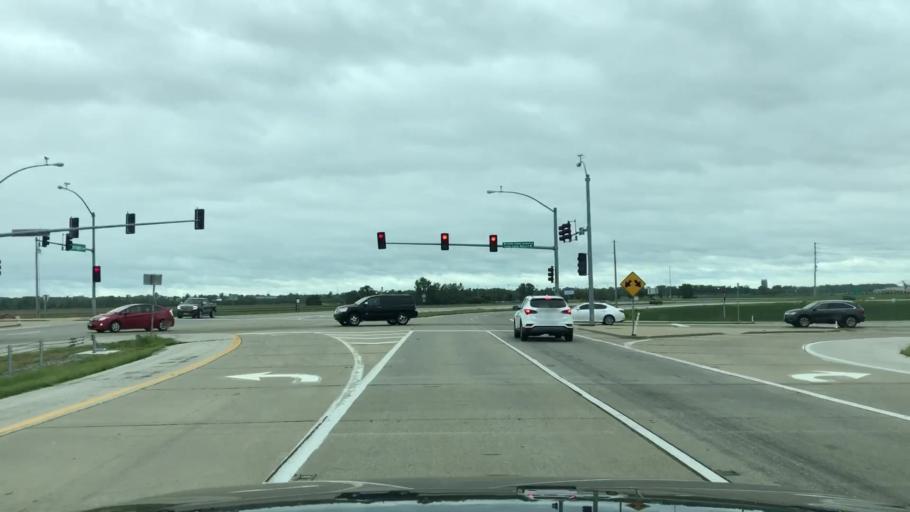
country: US
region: Missouri
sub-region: Saint Charles County
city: Saint Charles
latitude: 38.7244
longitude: -90.4984
